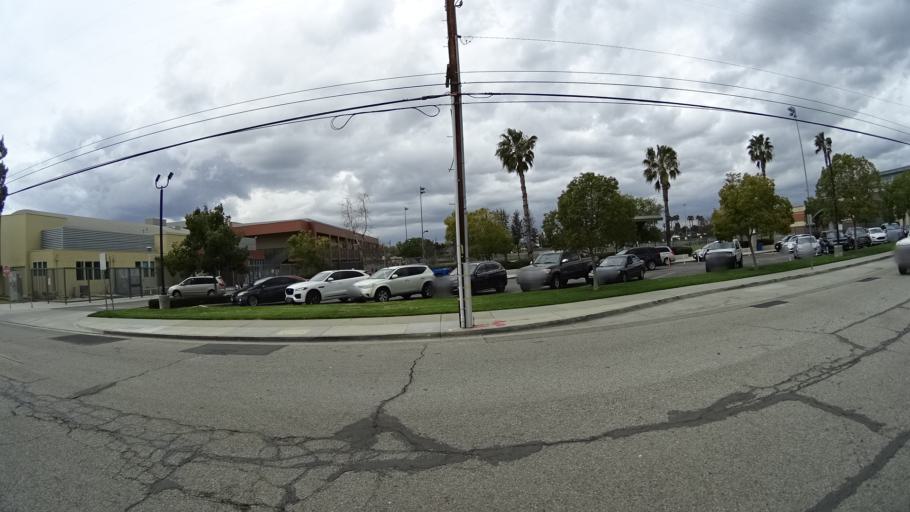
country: US
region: California
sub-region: Orange County
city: Placentia
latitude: 33.8586
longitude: -117.8723
